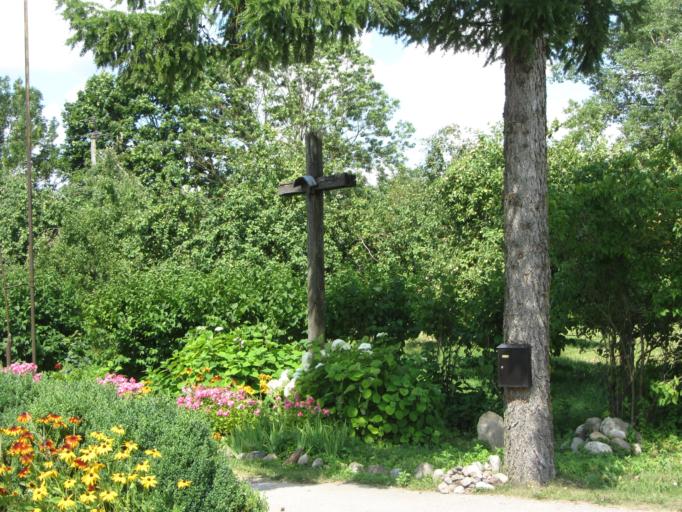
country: LT
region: Vilnius County
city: Ukmerge
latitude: 55.1123
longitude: 24.6883
